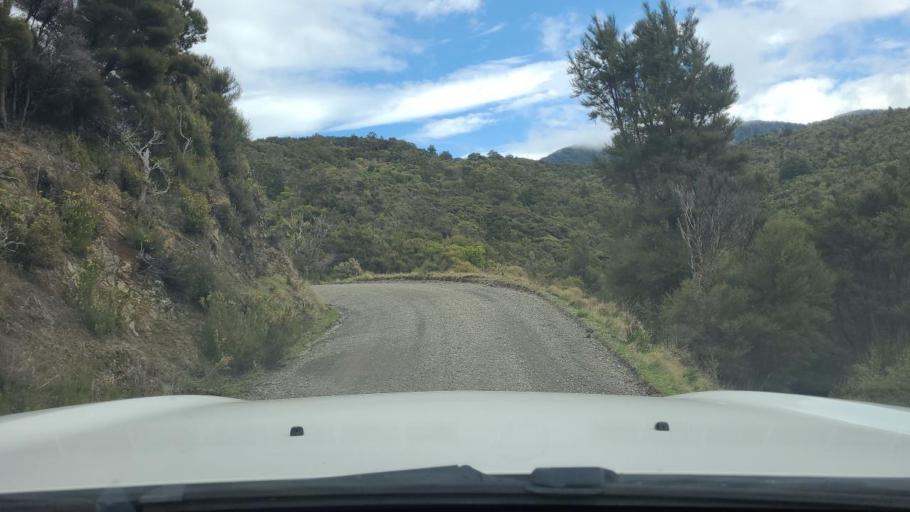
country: NZ
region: Wellington
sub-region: South Wairarapa District
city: Waipawa
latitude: -41.4063
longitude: 175.3642
